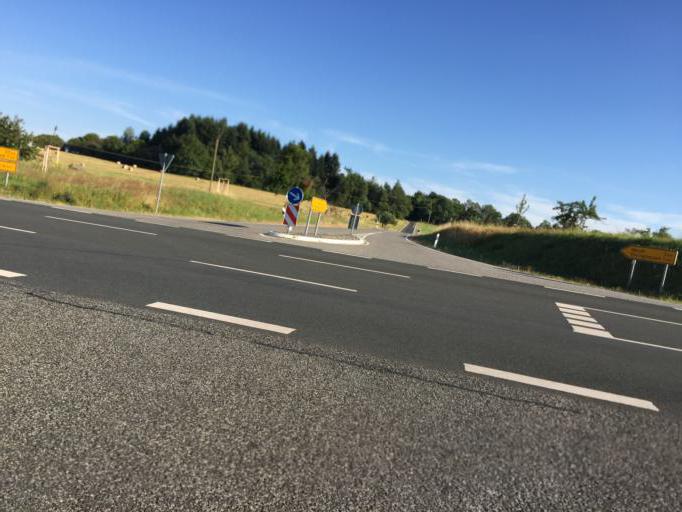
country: DE
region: Rheinland-Pfalz
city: Hartlingen
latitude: 50.5204
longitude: 7.8900
